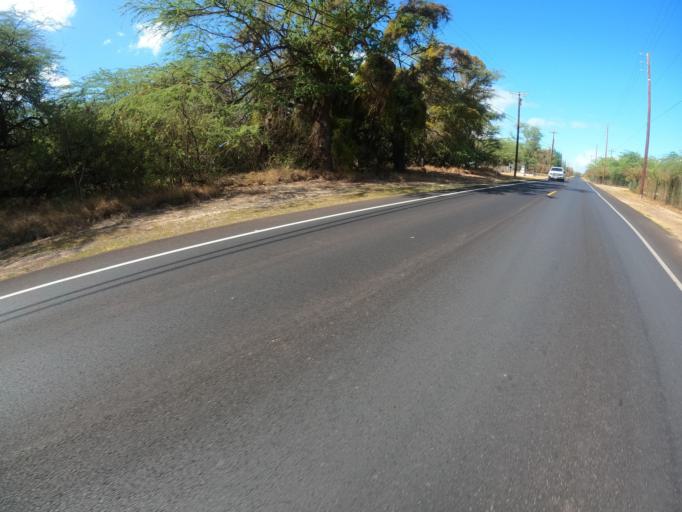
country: US
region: Hawaii
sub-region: Honolulu County
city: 'Ewa Villages
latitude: 21.3089
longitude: -158.0563
